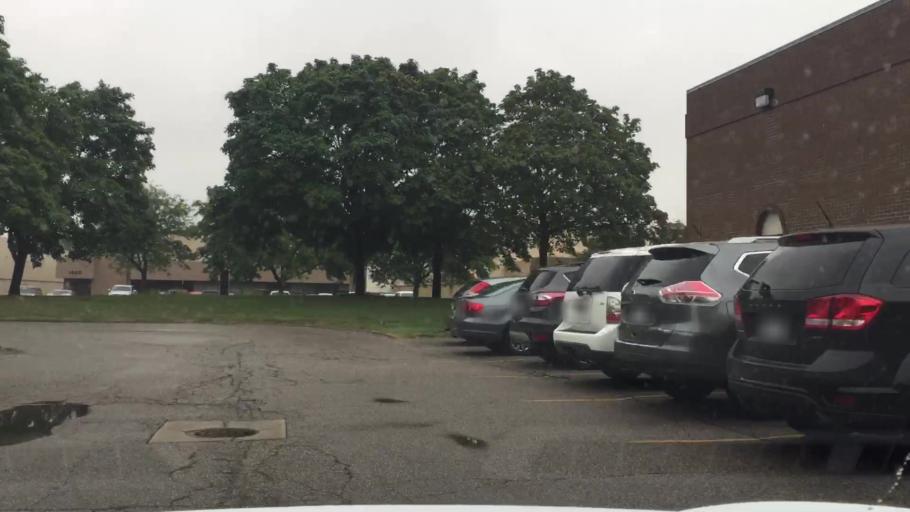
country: US
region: Michigan
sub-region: Oakland County
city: Clawson
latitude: 42.5451
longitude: -83.1255
